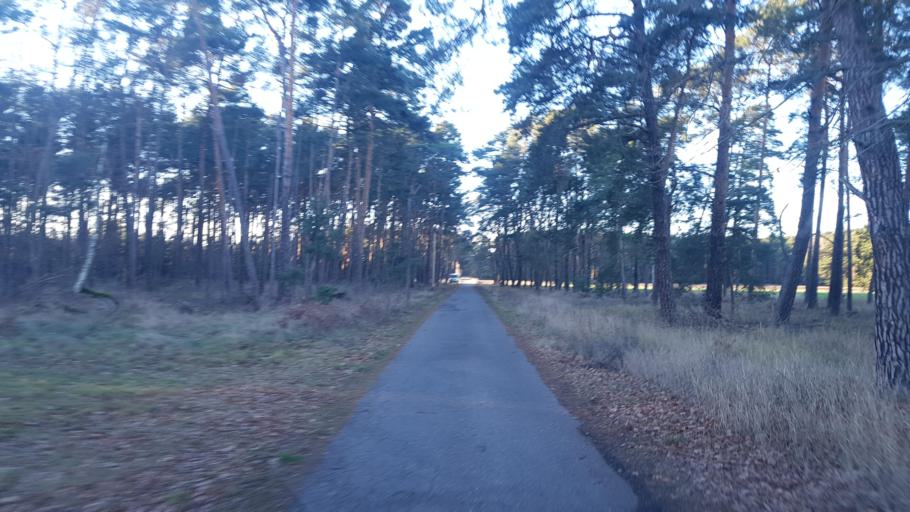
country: DE
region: Brandenburg
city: Peitz
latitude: 51.8857
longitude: 14.4010
